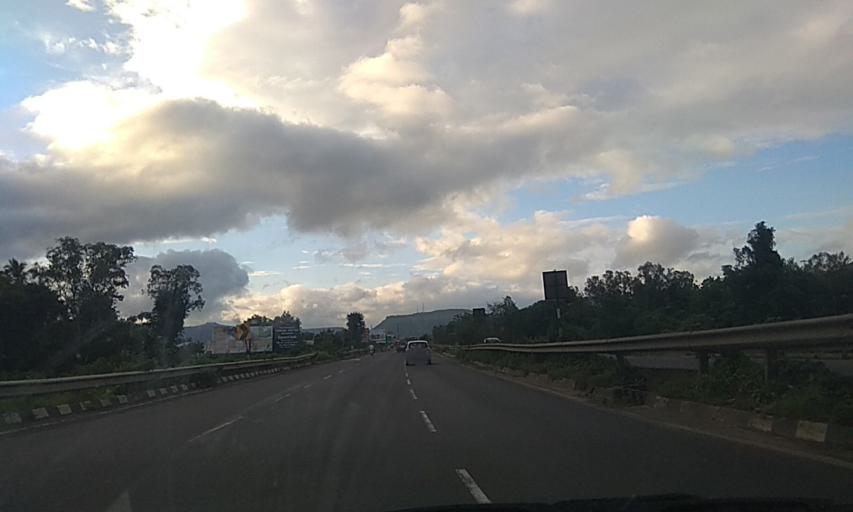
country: IN
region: Maharashtra
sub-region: Satara Division
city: Satara
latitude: 17.6188
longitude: 74.0202
